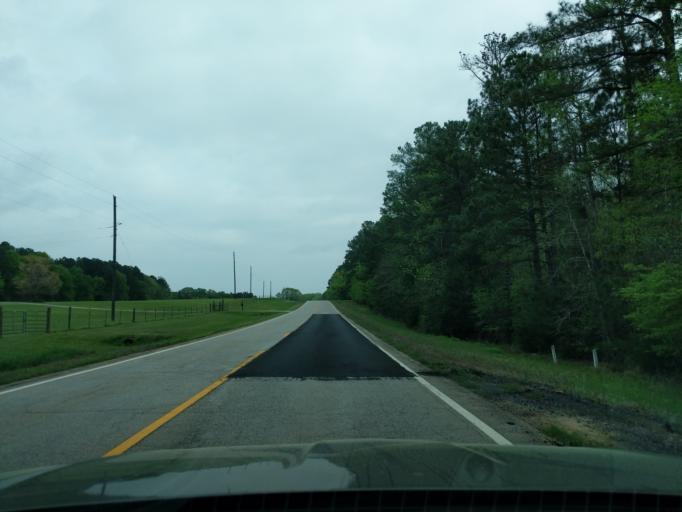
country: US
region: Georgia
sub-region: Lincoln County
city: Lincolnton
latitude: 33.7837
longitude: -82.3814
